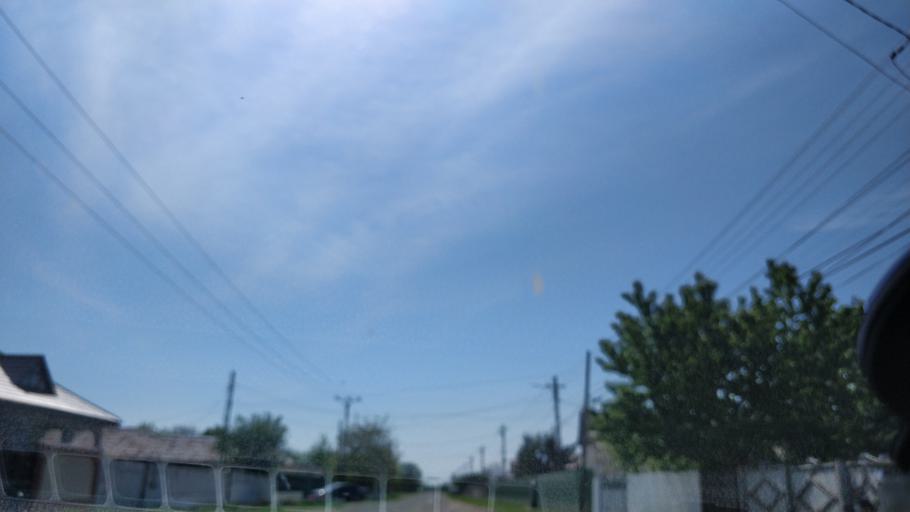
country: RO
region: Vrancea
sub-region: Comuna Suraia
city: Suraia
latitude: 45.6680
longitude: 27.3898
